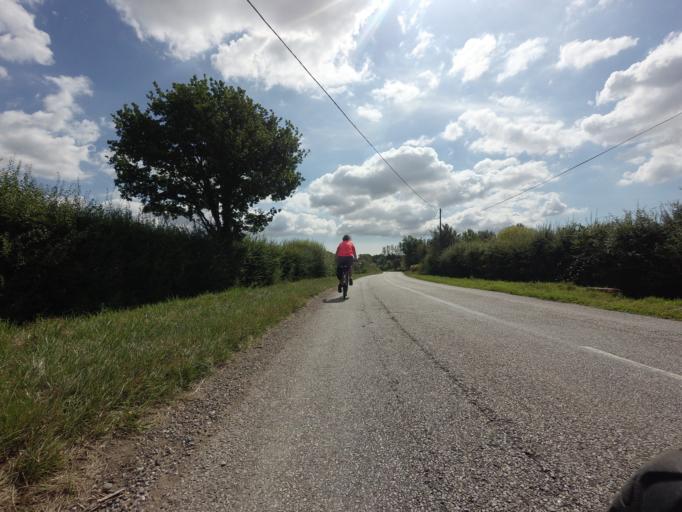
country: GB
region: England
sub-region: Kent
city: Tenterden
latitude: 51.0731
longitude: 0.7388
